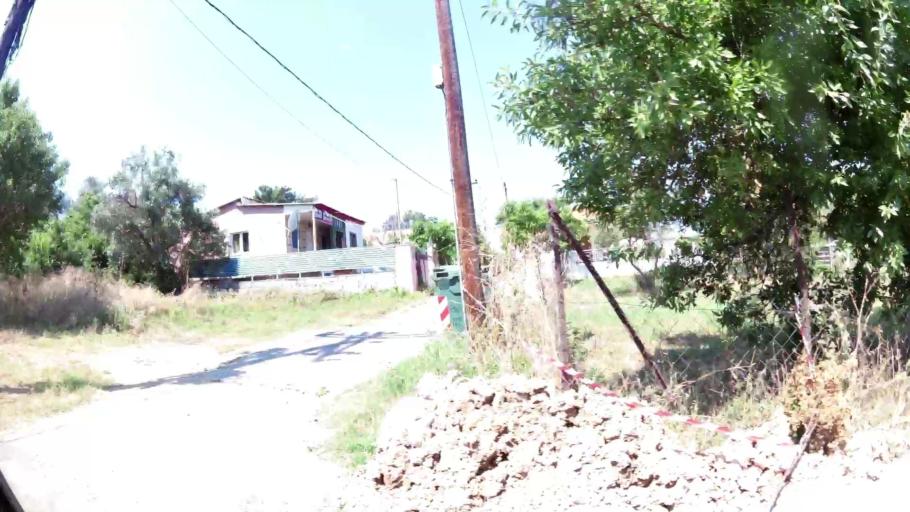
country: GR
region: Central Macedonia
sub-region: Nomos Thessalonikis
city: Neoi Epivates
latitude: 40.4970
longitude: 22.8940
